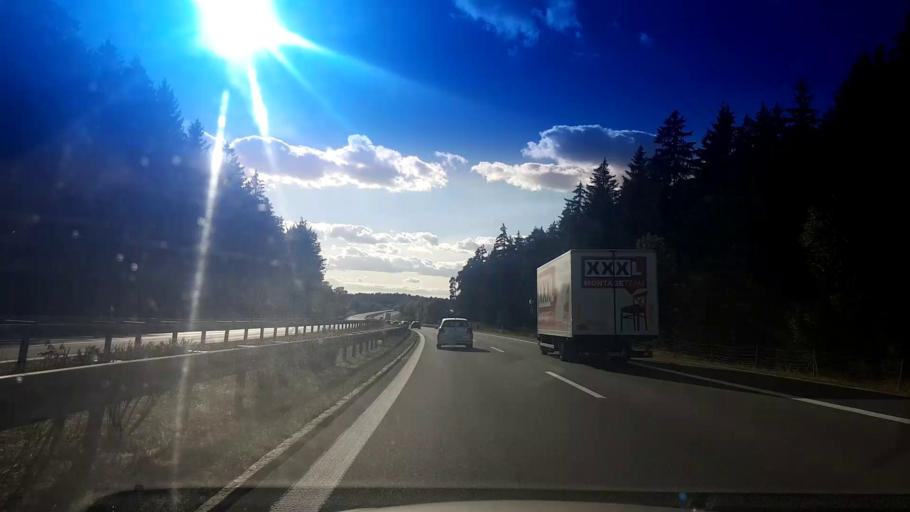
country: DE
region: Bavaria
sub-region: Upper Franconia
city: Wonsees
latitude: 50.0076
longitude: 11.2742
